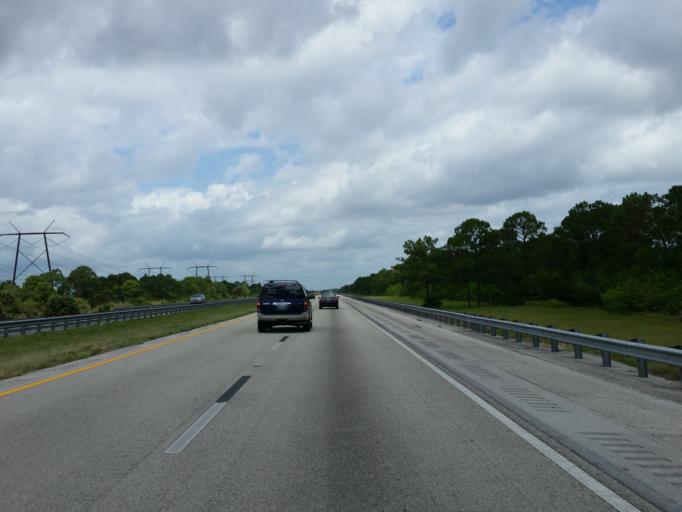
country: US
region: Florida
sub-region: Indian River County
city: West Vero Corridor
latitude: 27.5393
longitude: -80.6174
